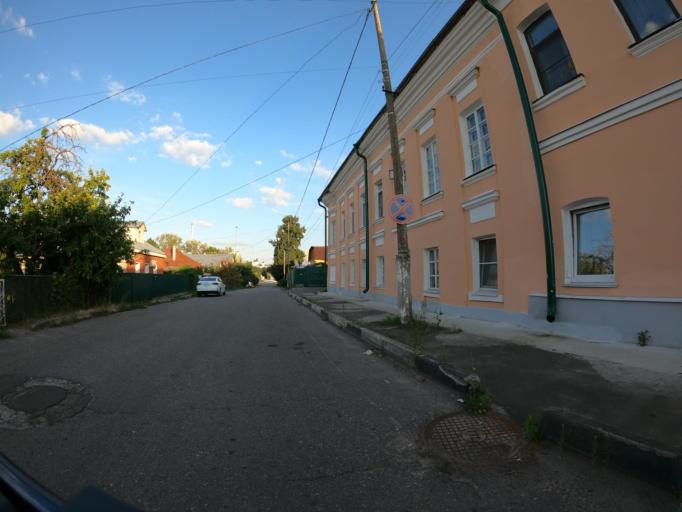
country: RU
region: Moskovskaya
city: Raduzhnyy
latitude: 55.1085
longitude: 38.7502
